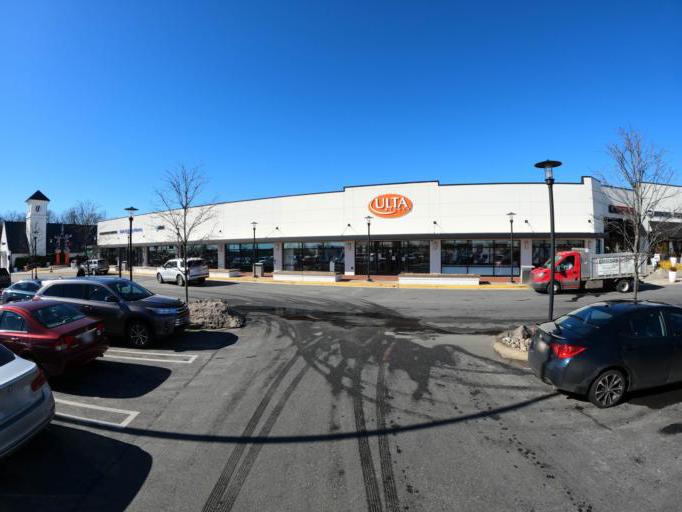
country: US
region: Maryland
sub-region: Montgomery County
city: Germantown
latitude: 39.2032
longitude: -77.2480
